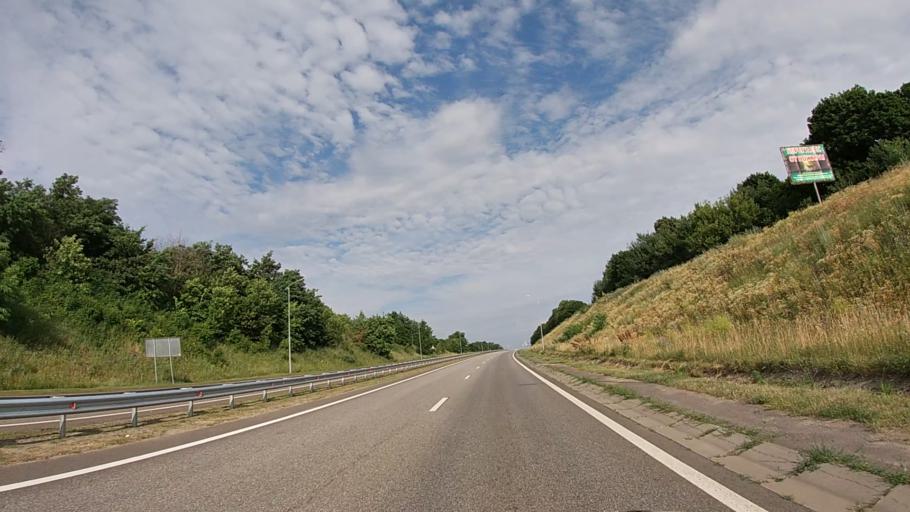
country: RU
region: Belgorod
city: Tomarovka
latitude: 50.6622
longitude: 36.3352
